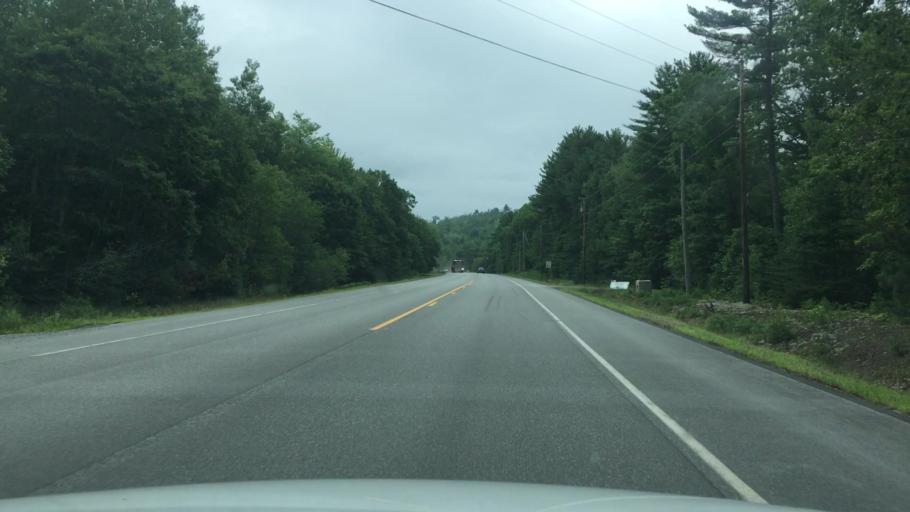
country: US
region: Maine
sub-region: Penobscot County
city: Bradley
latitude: 44.8246
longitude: -68.4853
